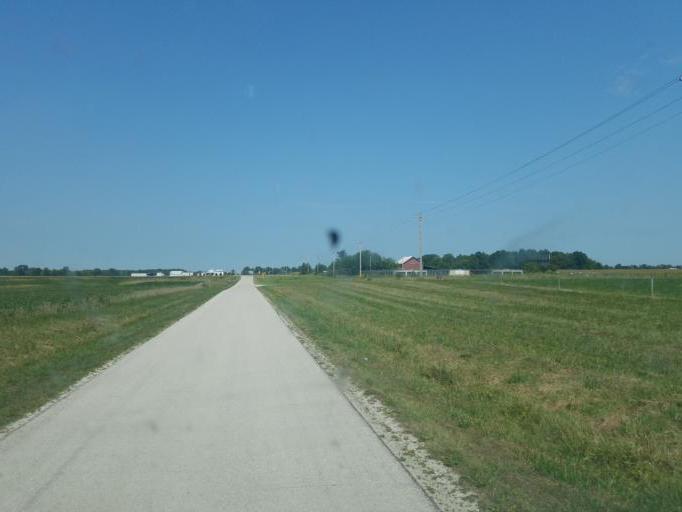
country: US
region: Ohio
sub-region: Crawford County
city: Bucyrus
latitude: 40.8065
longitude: -83.1122
